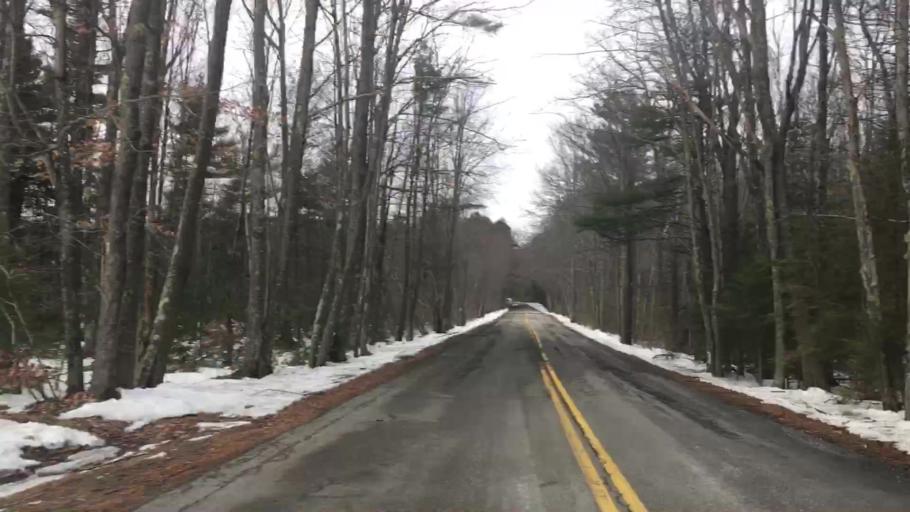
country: US
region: Maine
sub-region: York County
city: Wells Beach Station
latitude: 43.3397
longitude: -70.6074
